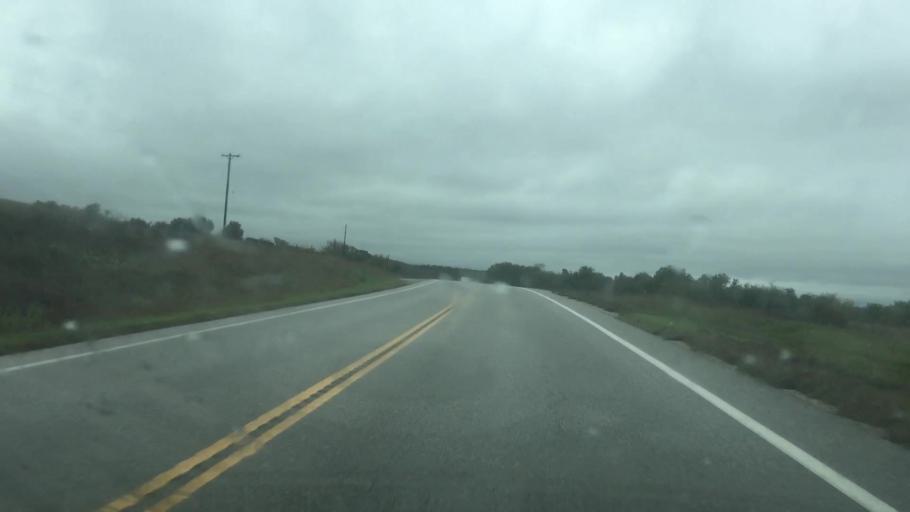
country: US
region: Kansas
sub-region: Anderson County
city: Garnett
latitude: 38.3863
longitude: -95.1099
